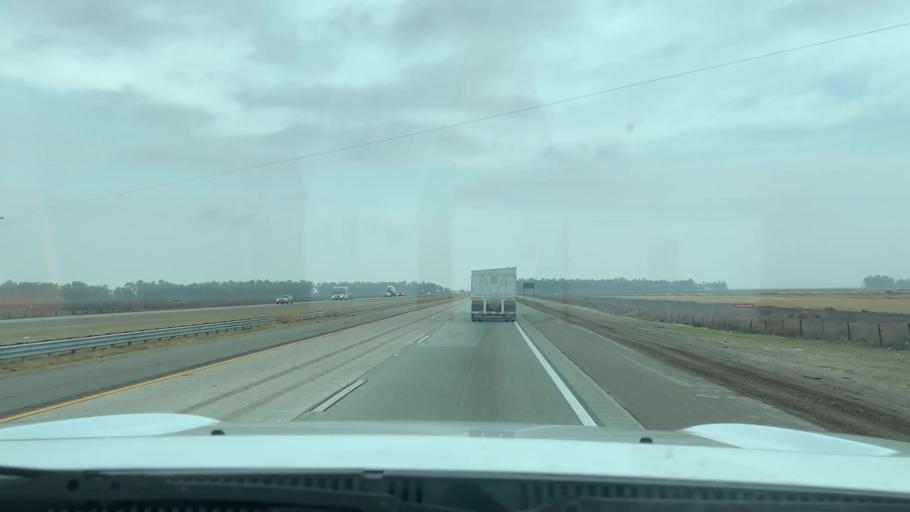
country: US
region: California
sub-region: Kern County
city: Lost Hills
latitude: 35.5868
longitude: -119.6270
